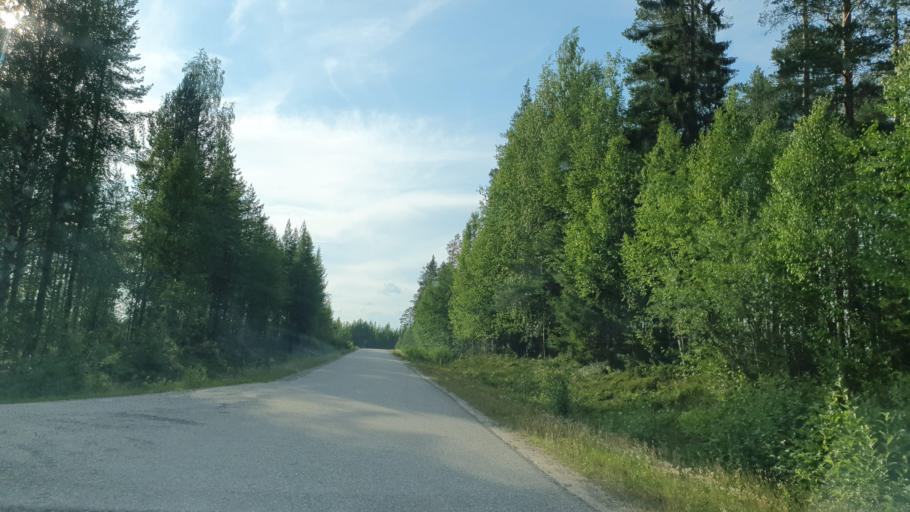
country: FI
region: Kainuu
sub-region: Kehys-Kainuu
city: Kuhmo
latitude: 64.2846
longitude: 29.3889
